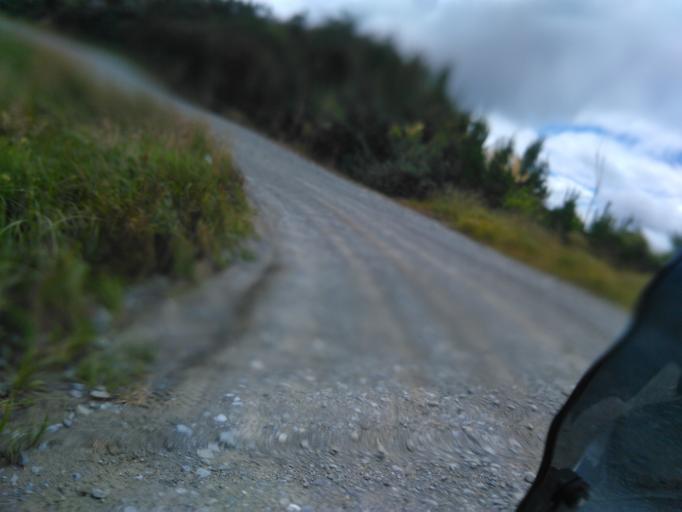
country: NZ
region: Gisborne
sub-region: Gisborne District
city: Gisborne
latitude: -38.1819
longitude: 178.1232
